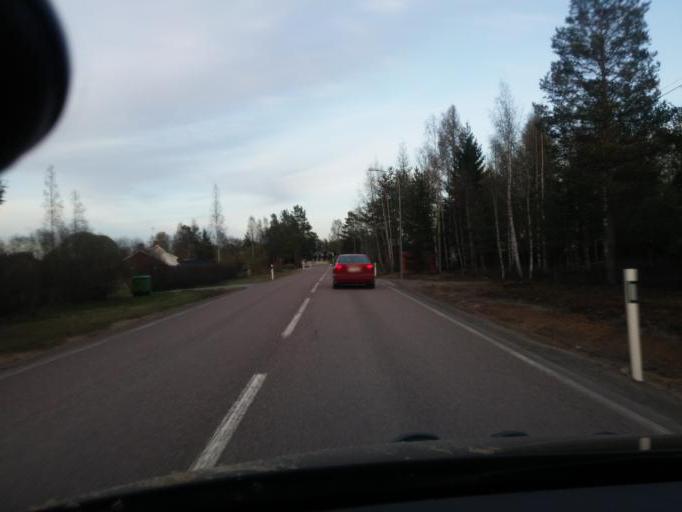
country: SE
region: Gaevleborg
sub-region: Ljusdals Kommun
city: Ljusdal
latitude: 61.8358
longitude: 16.0123
